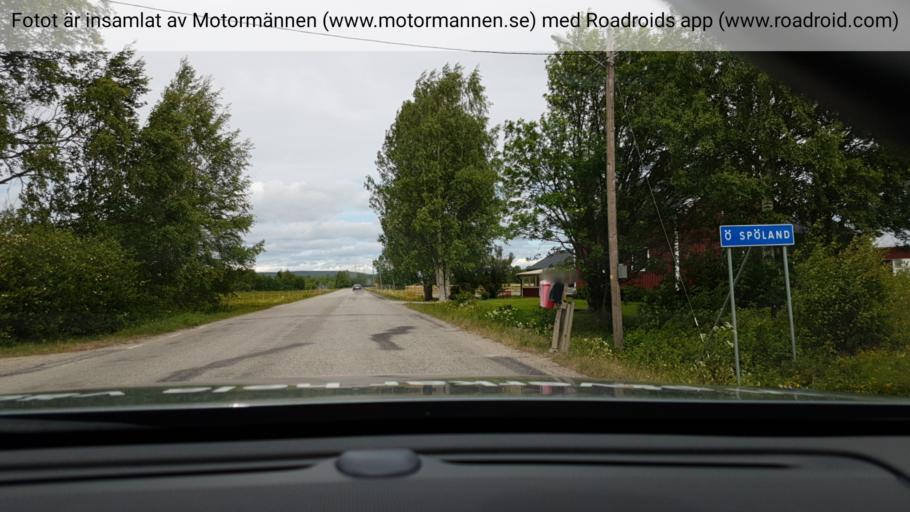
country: SE
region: Vaesterbotten
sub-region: Vannas Kommun
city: Vannasby
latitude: 63.9264
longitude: 19.8542
